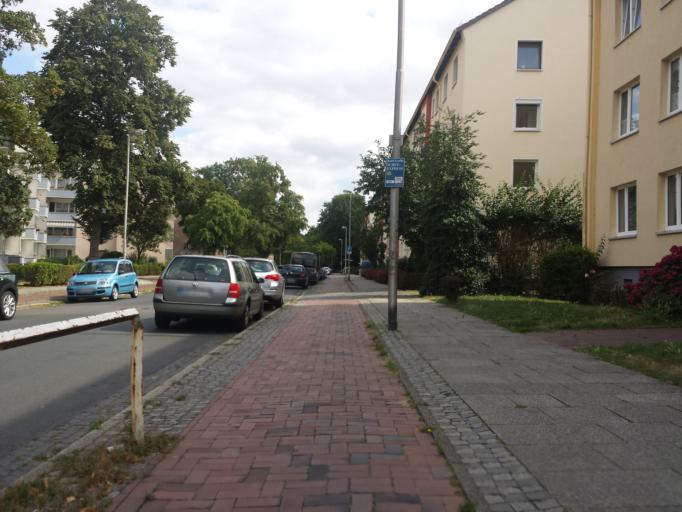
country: DE
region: Bremen
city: Bremen
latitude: 53.0620
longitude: 8.7963
